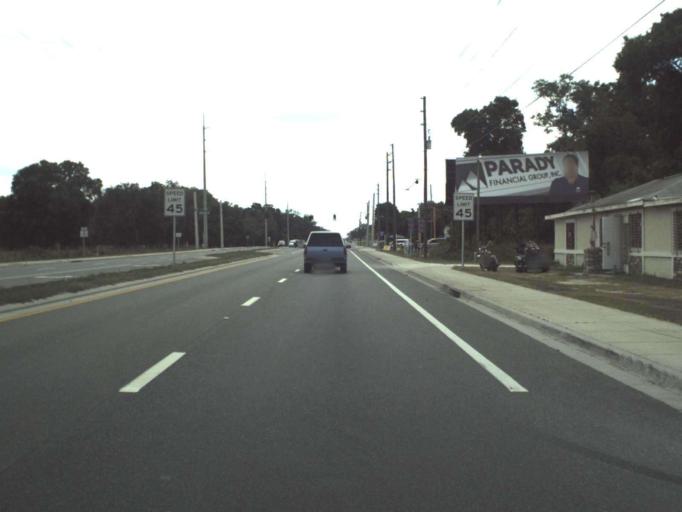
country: US
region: Florida
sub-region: Sumter County
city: Wildwood
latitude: 28.8819
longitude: -82.0370
